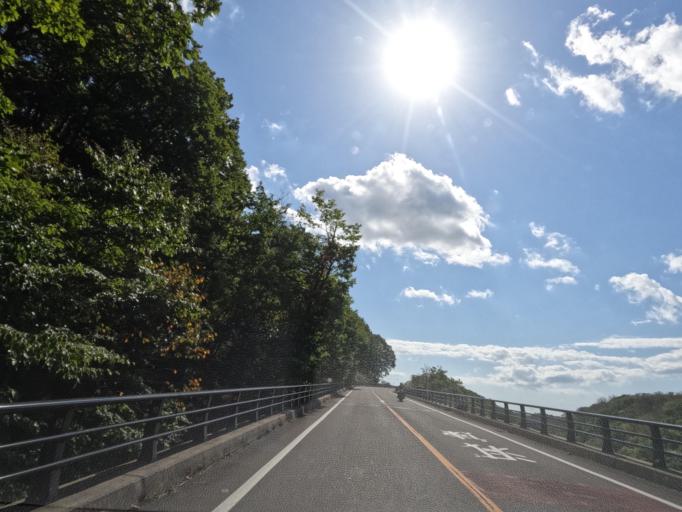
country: JP
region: Hokkaido
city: Shiraoi
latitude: 42.4799
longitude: 141.1452
